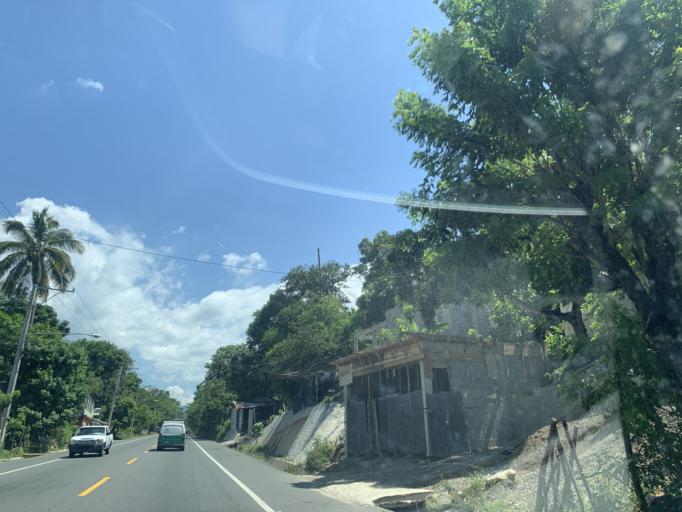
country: DO
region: Puerto Plata
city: Altamira
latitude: 19.7117
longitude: -70.8357
